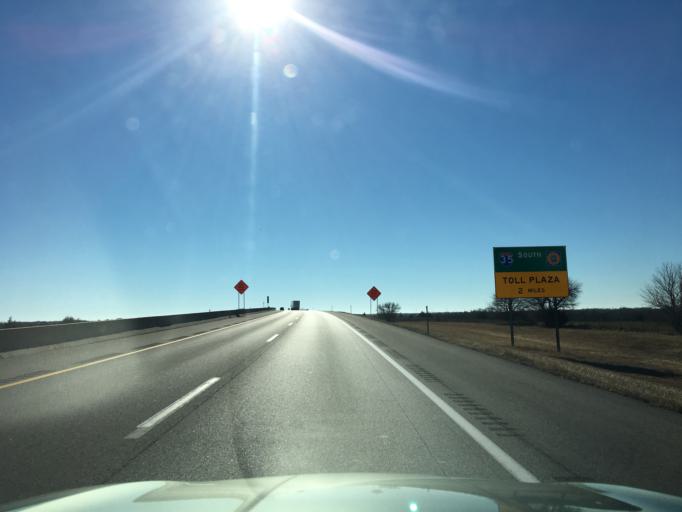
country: US
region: Kansas
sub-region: Sumner County
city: Wellington
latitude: 37.2689
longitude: -97.3404
